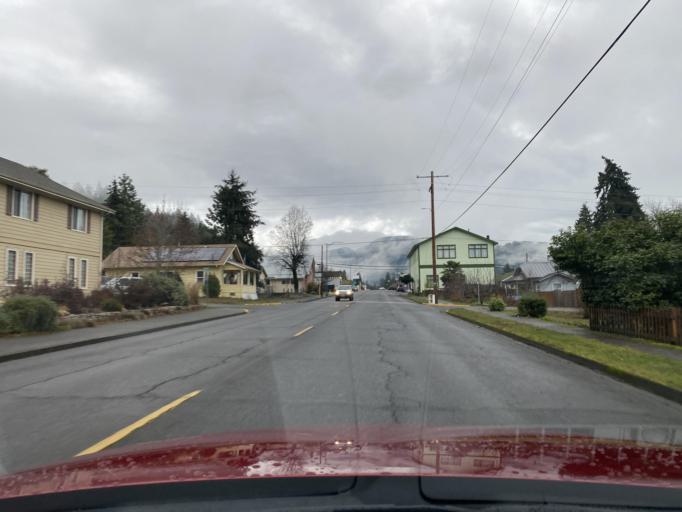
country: US
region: Oregon
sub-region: Lane County
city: Oakridge
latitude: 43.7479
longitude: -122.4628
